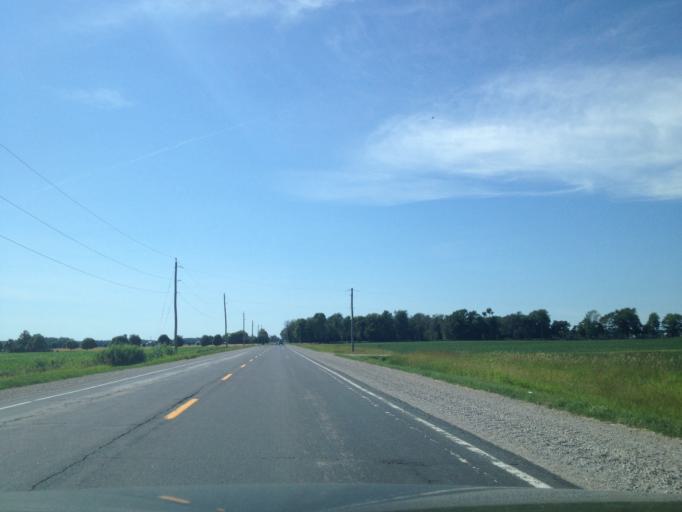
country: CA
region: Ontario
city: Stratford
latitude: 43.4914
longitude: -80.8527
